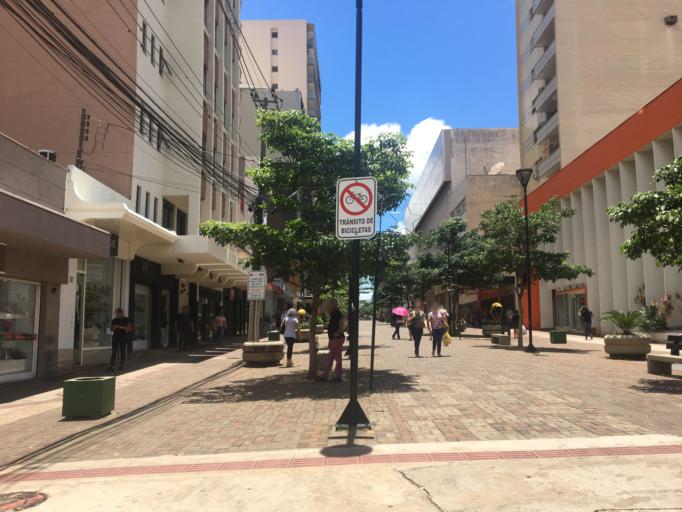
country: BR
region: Parana
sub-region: Londrina
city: Londrina
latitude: -23.3109
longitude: -51.1627
